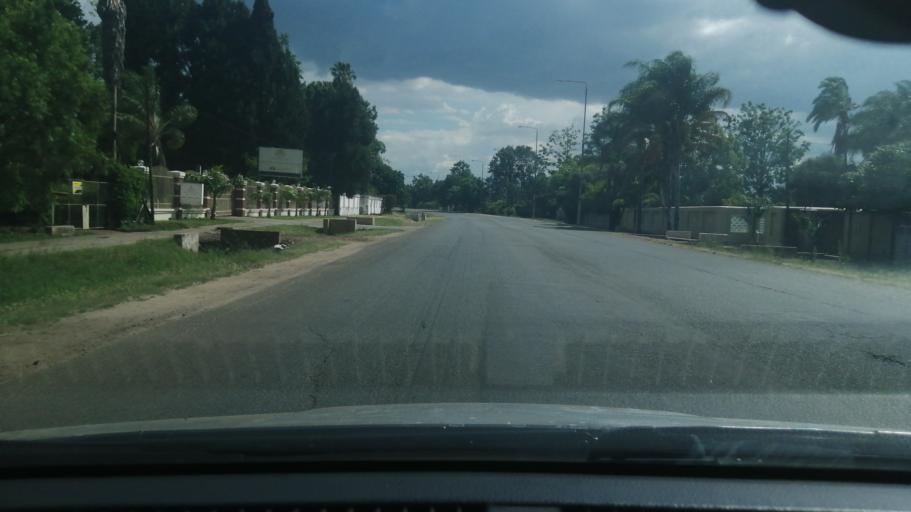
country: ZW
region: Harare
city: Harare
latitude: -17.8168
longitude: 31.0923
